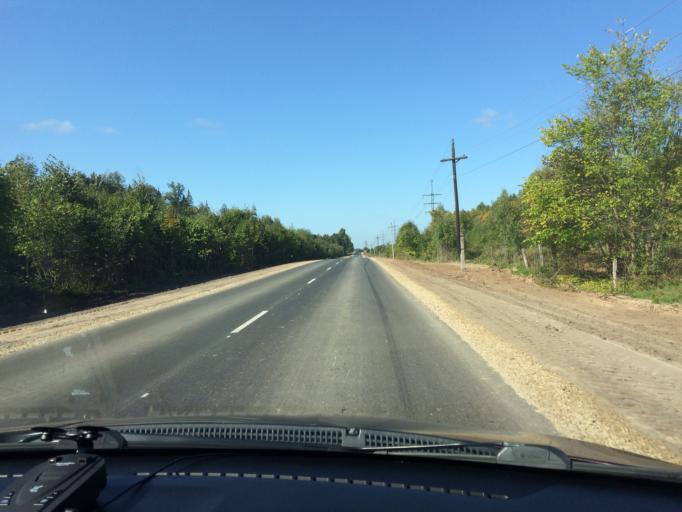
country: RU
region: Mariy-El
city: Sovetskiy
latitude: 56.5461
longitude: 48.4211
